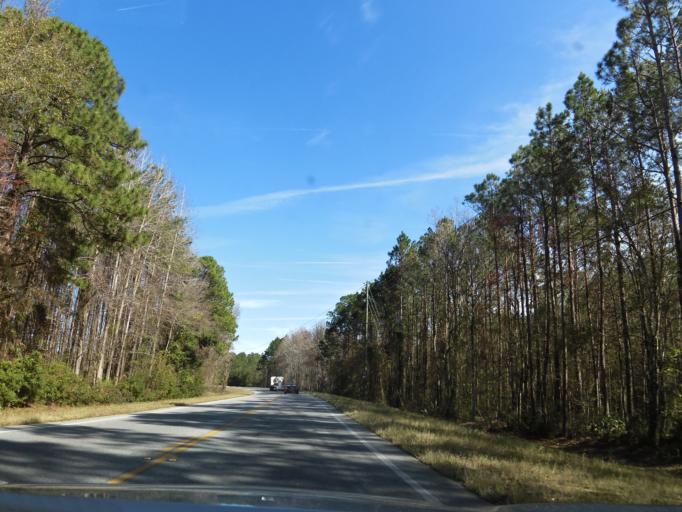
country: US
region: Georgia
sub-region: Glynn County
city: Dock Junction
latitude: 31.2754
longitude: -81.5232
